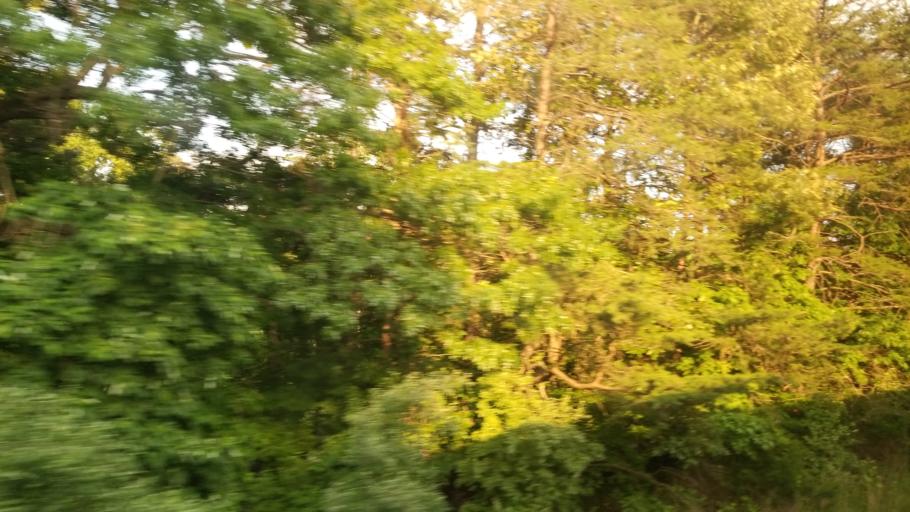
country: US
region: Virginia
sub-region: Prince William County
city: Yorkshire
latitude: 38.7739
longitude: -77.4348
